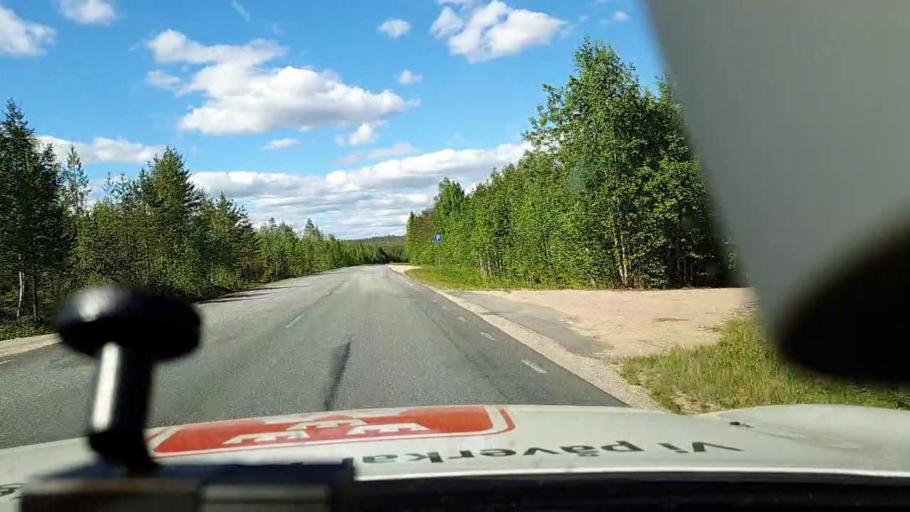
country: FI
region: Lapland
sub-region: Torniolaakso
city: Ylitornio
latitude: 66.3164
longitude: 23.6196
